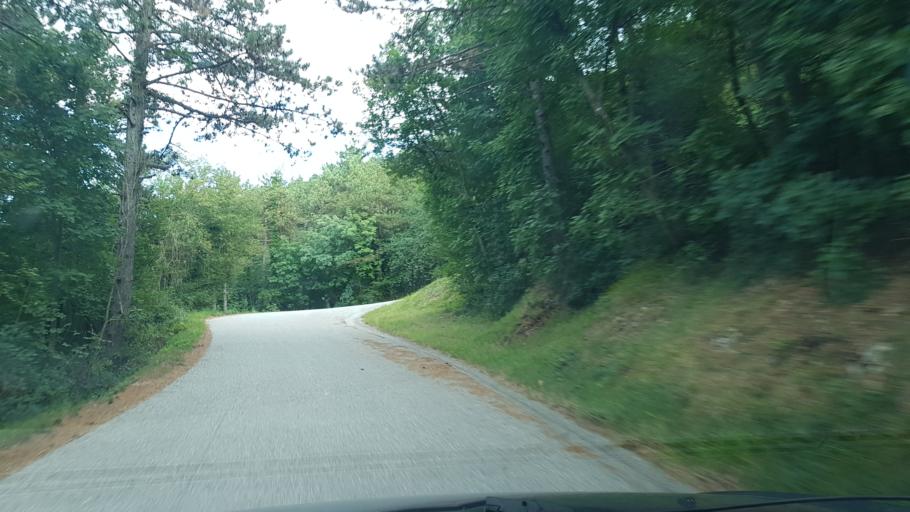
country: SI
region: Rence-Vogrsko
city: Rence
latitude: 45.8706
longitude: 13.6573
